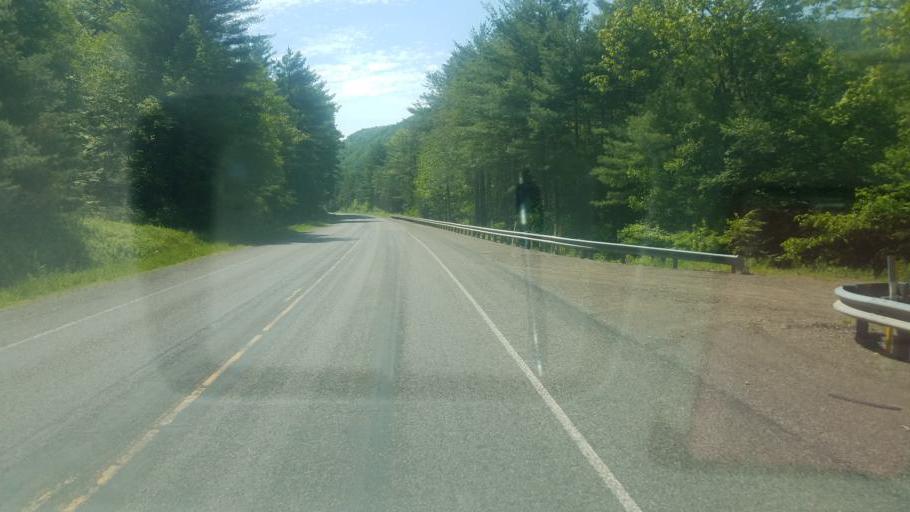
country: US
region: Pennsylvania
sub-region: Potter County
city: Galeton
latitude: 41.7472
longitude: -77.6718
